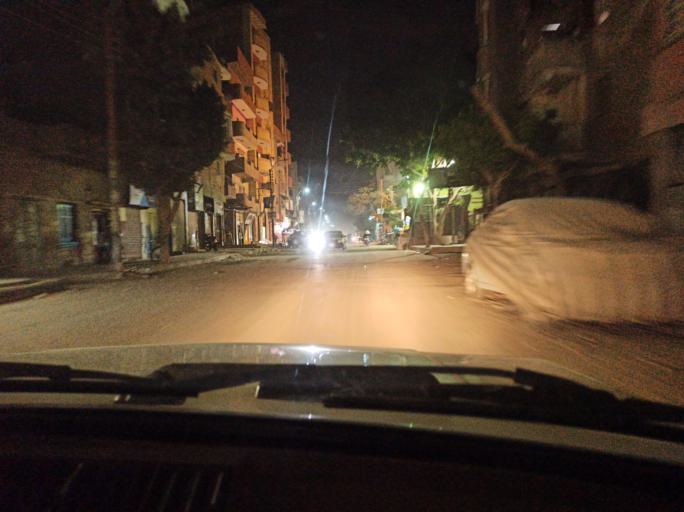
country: EG
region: Muhafazat Bani Suwayf
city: Bani Suwayf
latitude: 29.0777
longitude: 31.0891
